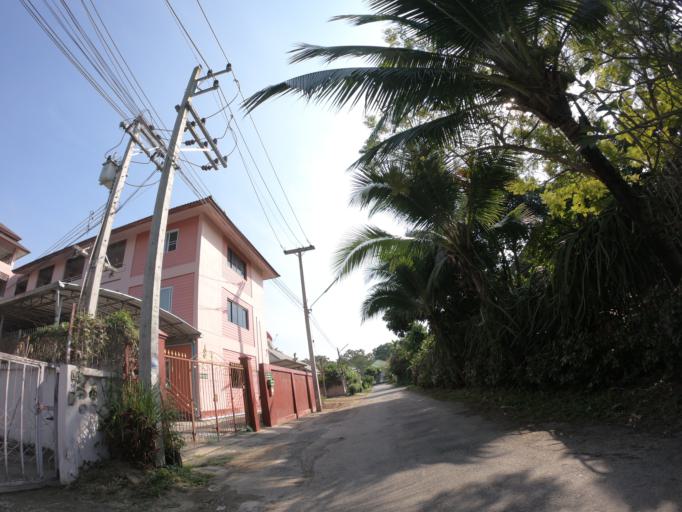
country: TH
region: Chiang Mai
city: Chiang Mai
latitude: 18.8237
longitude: 98.9887
